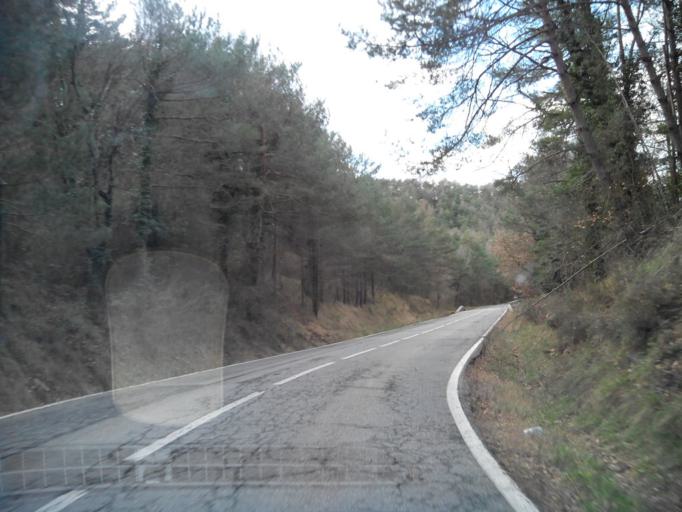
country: ES
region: Catalonia
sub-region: Provincia de Barcelona
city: Olost
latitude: 41.9678
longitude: 2.1368
